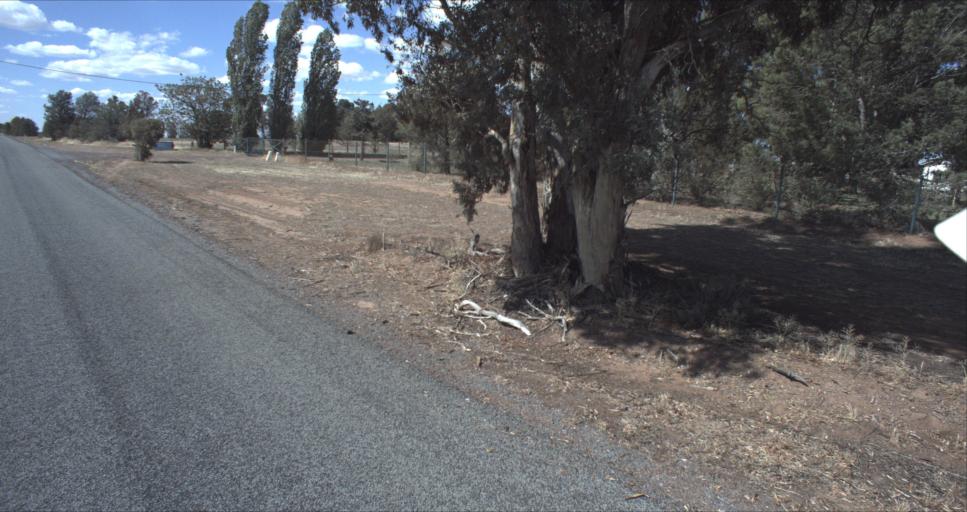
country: AU
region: New South Wales
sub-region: Leeton
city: Leeton
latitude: -34.4850
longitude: 146.2484
